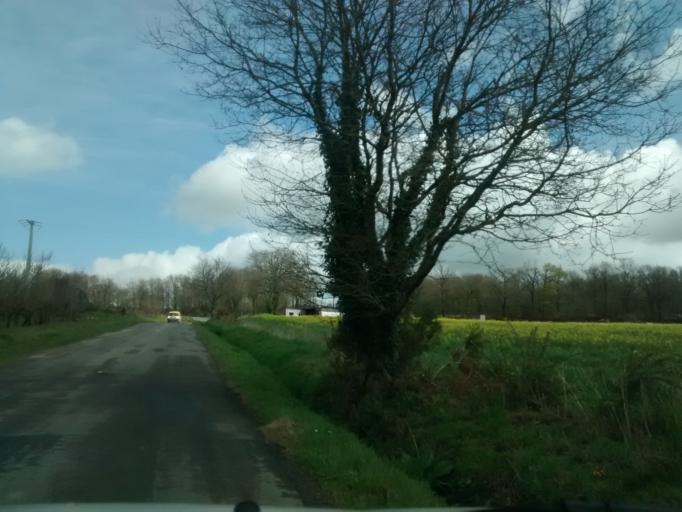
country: FR
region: Brittany
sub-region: Departement d'Ille-et-Vilaine
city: Livre-sur-Changeon
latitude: 48.2057
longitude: -1.3563
